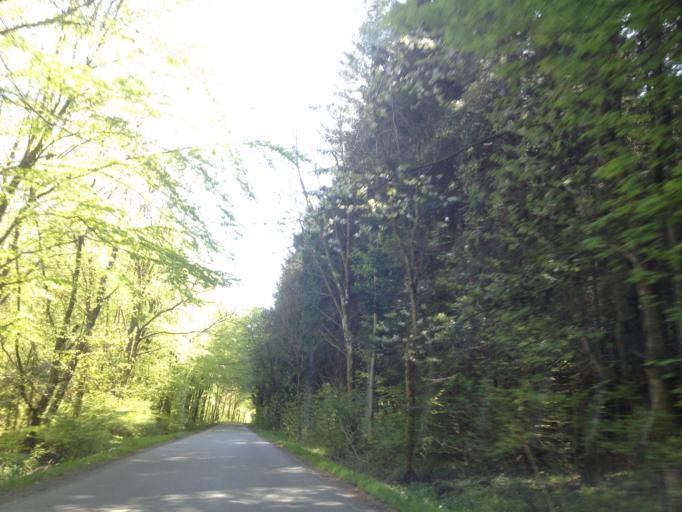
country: DK
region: Zealand
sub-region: Roskilde Kommune
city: Viby
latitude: 55.5263
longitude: 12.0154
